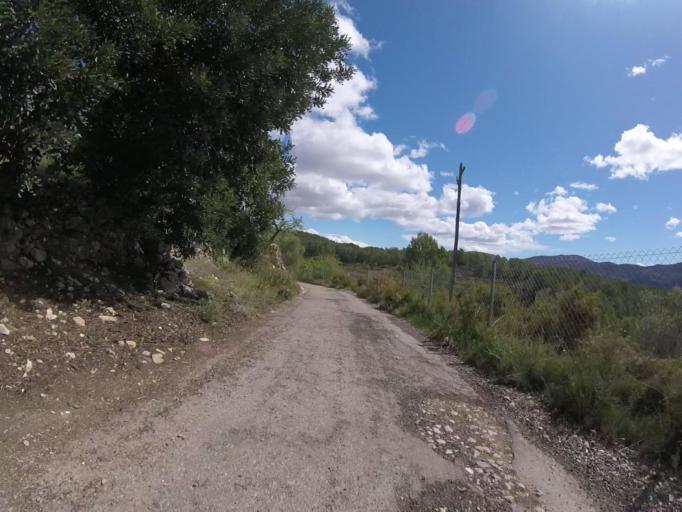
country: ES
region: Valencia
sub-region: Provincia de Castello
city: Sierra-Engarceran
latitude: 40.2689
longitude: -0.1001
